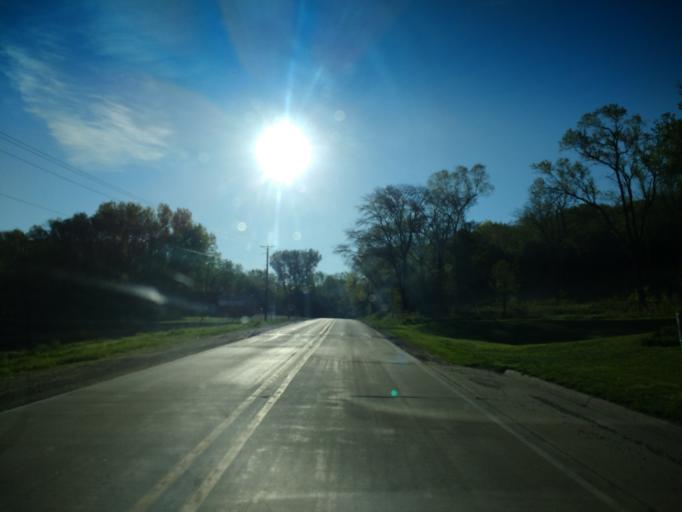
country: US
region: Iowa
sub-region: Harrison County
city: Missouri Valley
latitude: 41.4326
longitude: -95.8635
